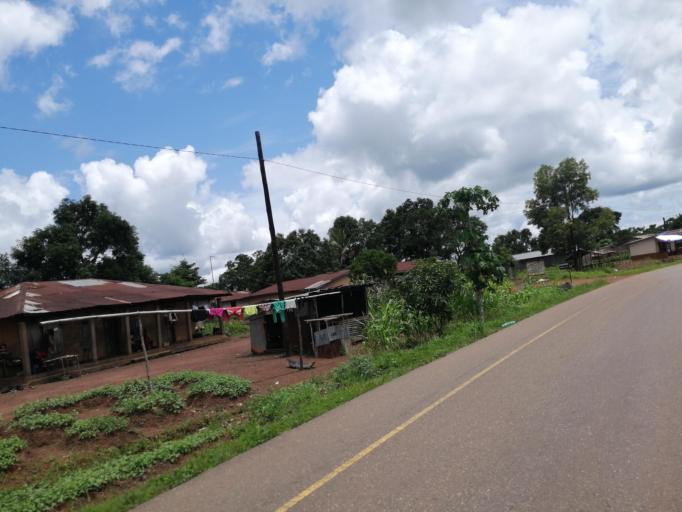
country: SL
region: Northern Province
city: Port Loko
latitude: 8.7774
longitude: -12.7958
